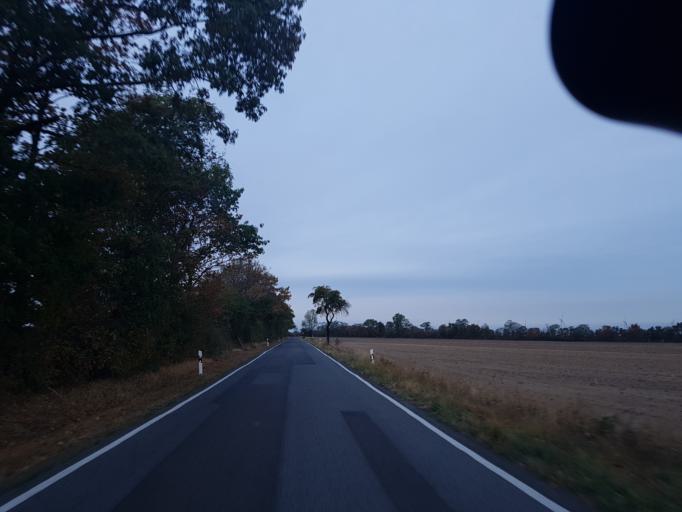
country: DE
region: Brandenburg
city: Muhlberg
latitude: 51.4985
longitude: 13.2475
